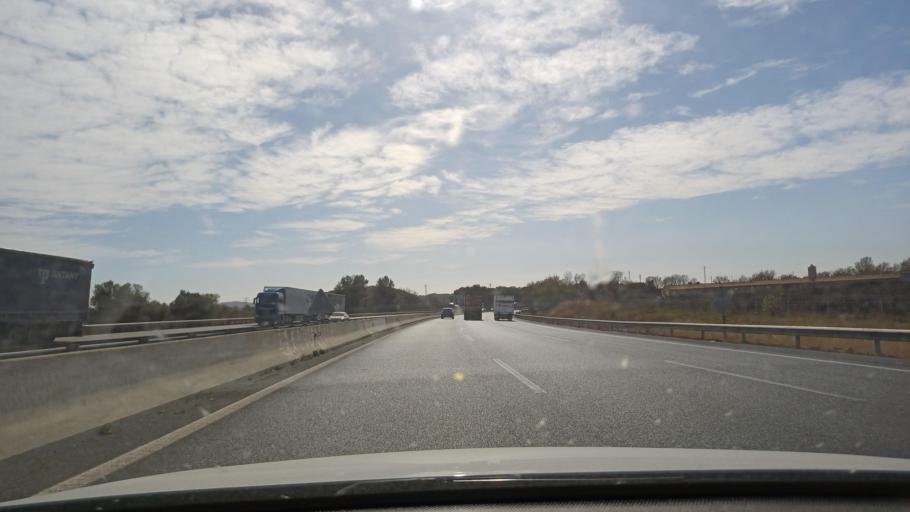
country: ES
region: Catalonia
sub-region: Provincia de Barcelona
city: Castellet
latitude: 41.3191
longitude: 1.6398
